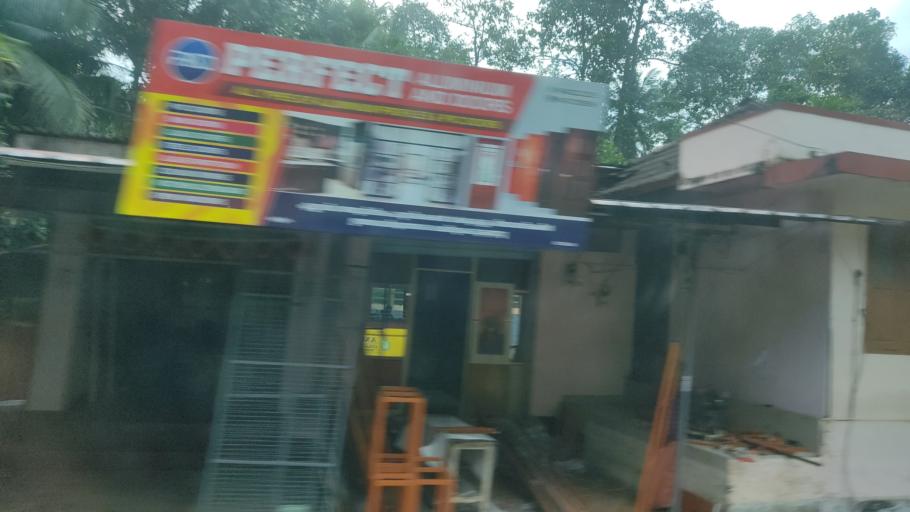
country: IN
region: Kerala
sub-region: Kottayam
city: Lalam
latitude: 9.6898
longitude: 76.6911
